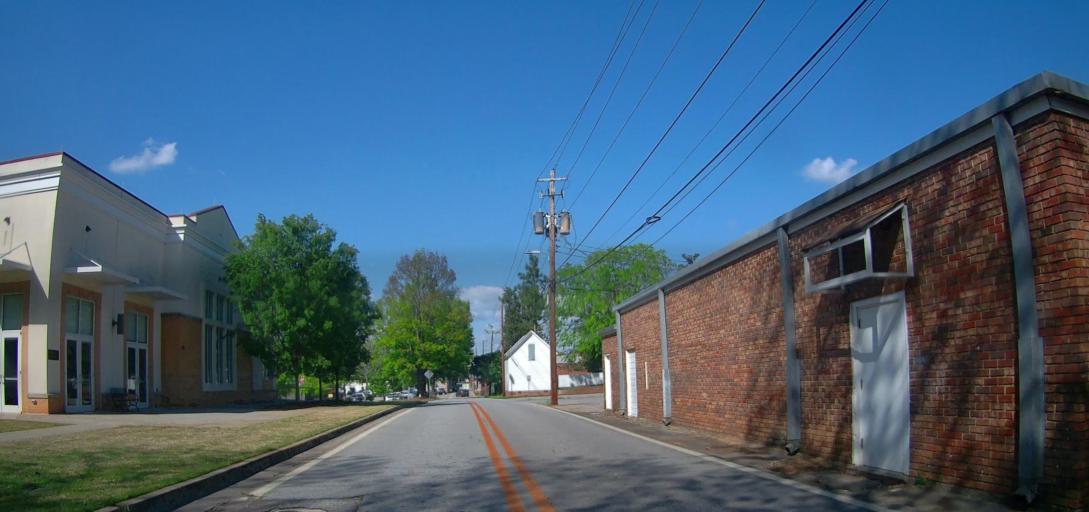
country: US
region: Georgia
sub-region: Morgan County
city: Madison
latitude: 33.5946
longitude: -83.4702
